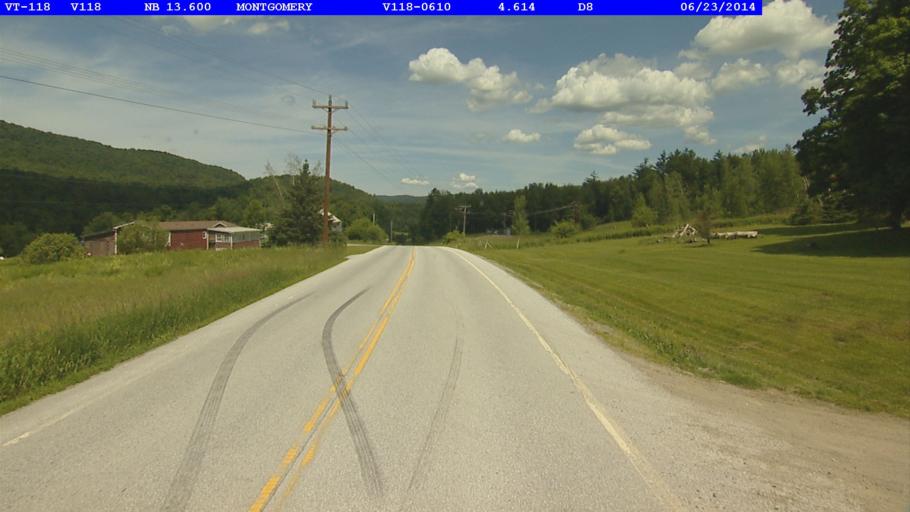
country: US
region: Vermont
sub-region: Franklin County
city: Richford
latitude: 44.8640
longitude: -72.6097
